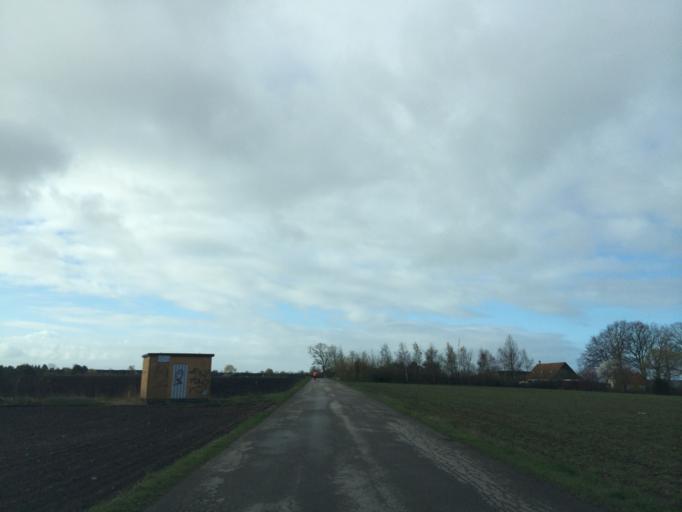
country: SE
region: Skane
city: Bjarred
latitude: 55.7369
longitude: 13.0182
